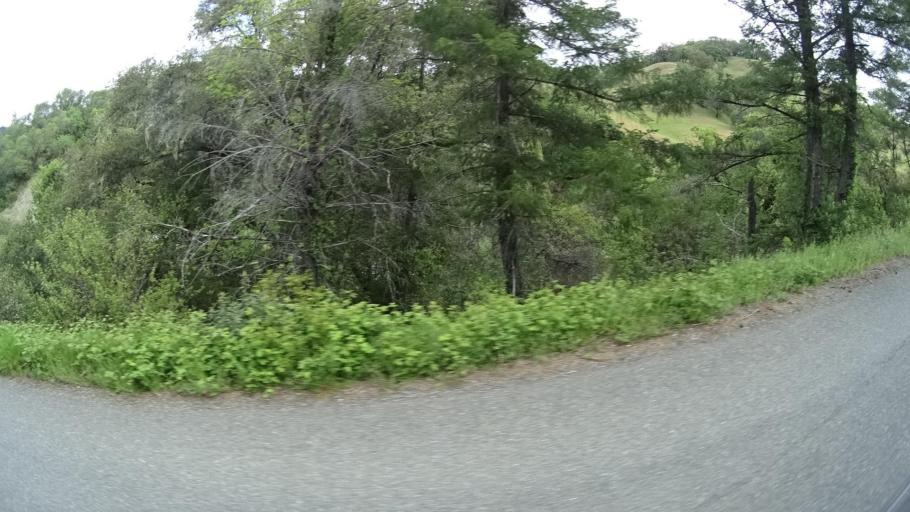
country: US
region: California
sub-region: Humboldt County
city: Redway
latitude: 40.1914
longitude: -123.5882
